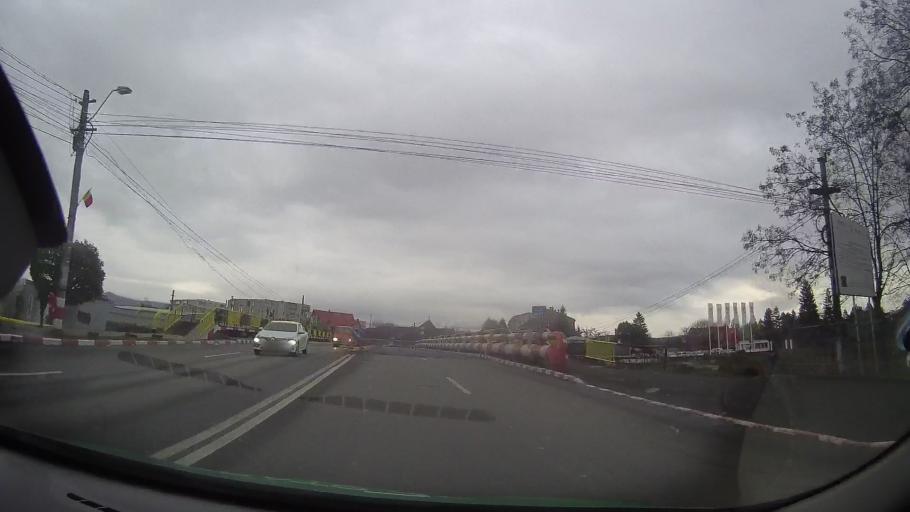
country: RO
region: Mures
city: Reghin-Sat
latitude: 46.7781
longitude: 24.7129
